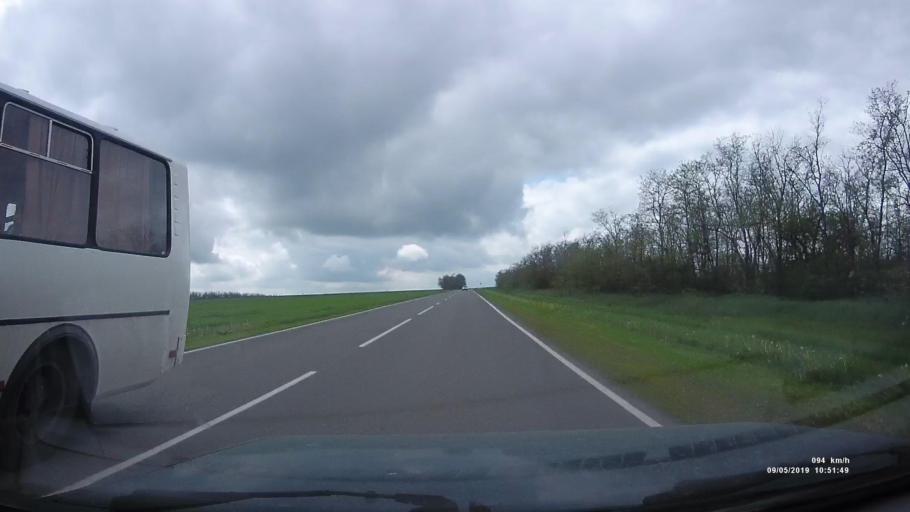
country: RU
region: Rostov
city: Peshkovo
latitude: 46.9090
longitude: 39.3542
